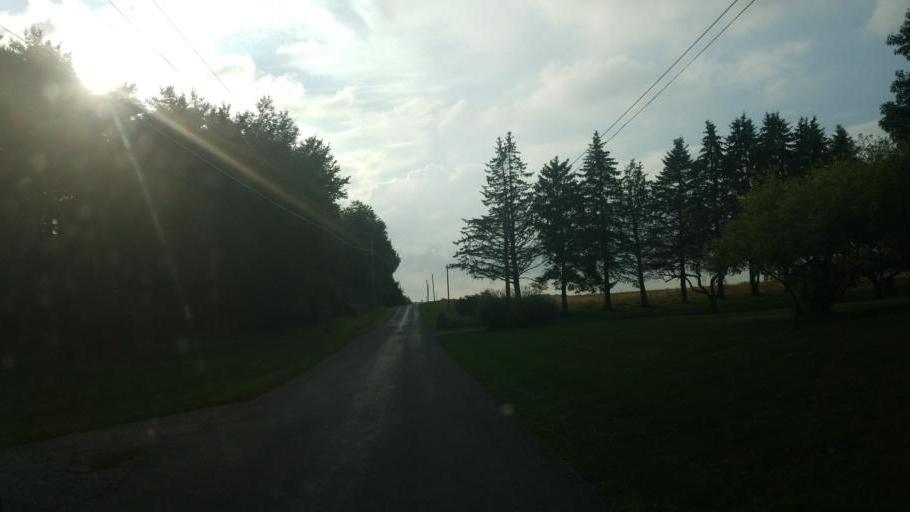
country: US
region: Ohio
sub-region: Wayne County
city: Wooster
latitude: 40.8254
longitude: -82.0378
